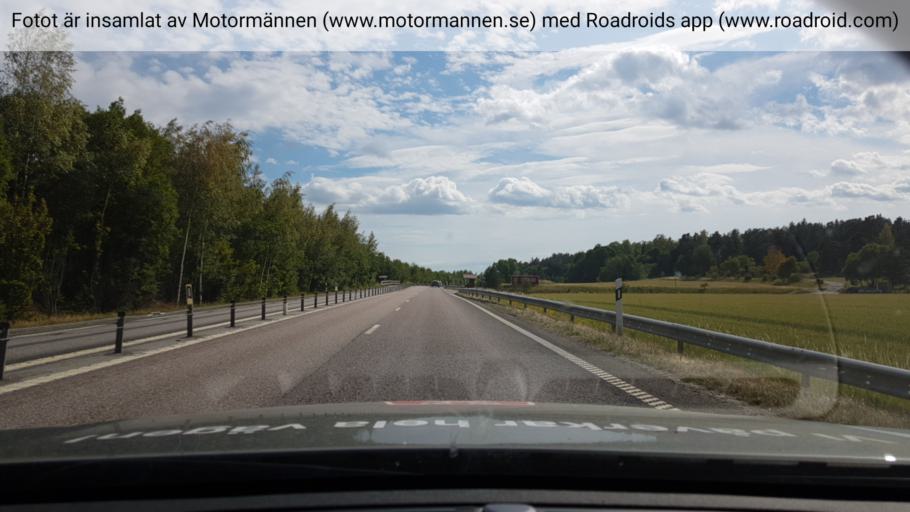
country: SE
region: Uppsala
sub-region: Enkopings Kommun
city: Orsundsbro
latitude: 59.7346
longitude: 17.3009
